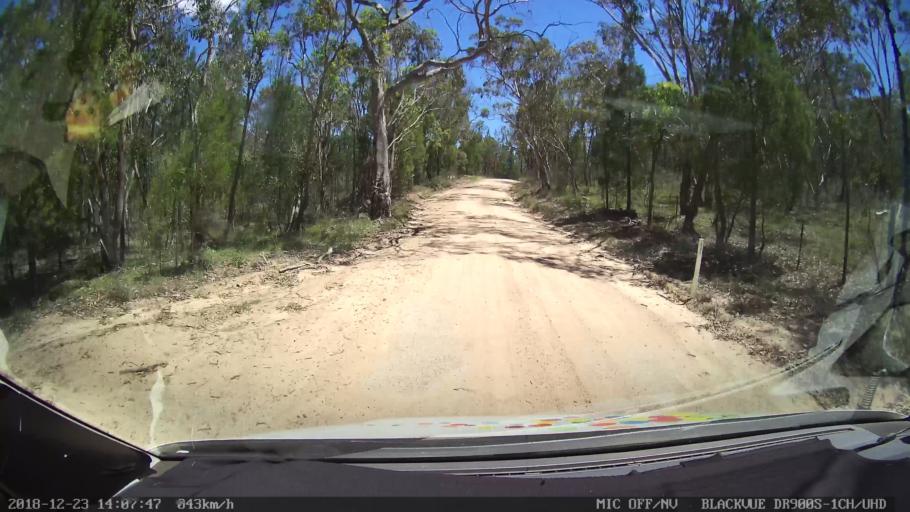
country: AU
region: New South Wales
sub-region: Tamworth Municipality
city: Manilla
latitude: -30.6383
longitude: 151.0710
